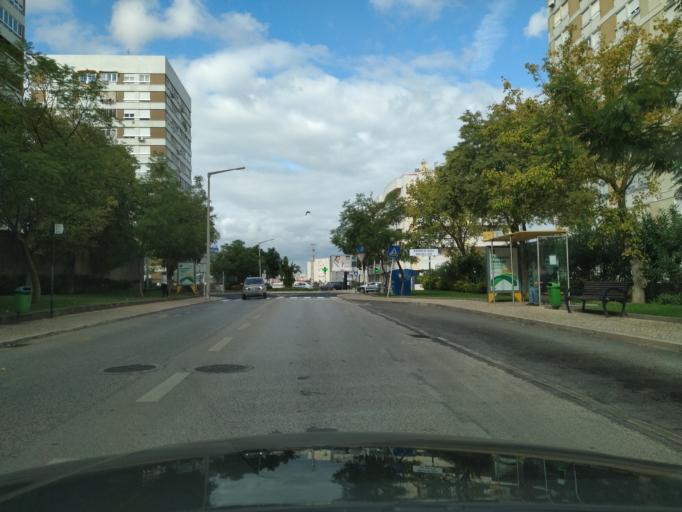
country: PT
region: Lisbon
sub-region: Loures
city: Sacavem
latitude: 38.7854
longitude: -9.1114
